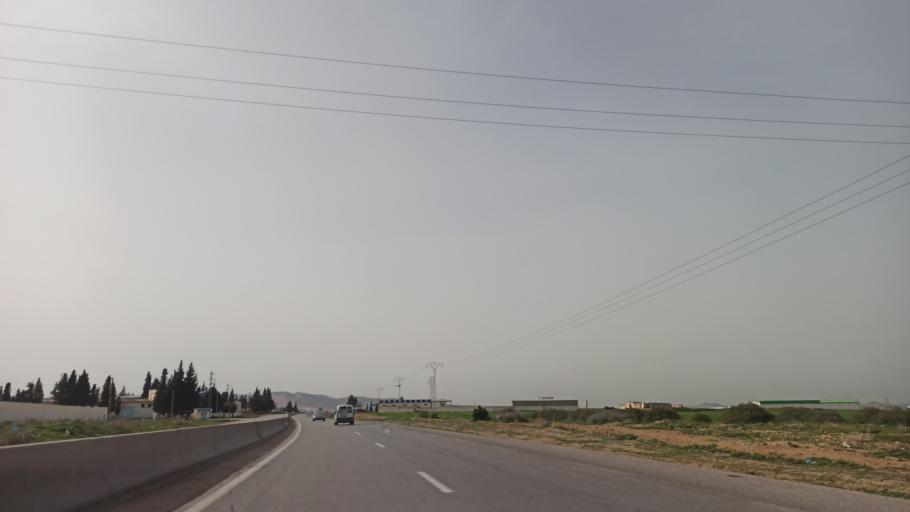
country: TN
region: Tunis
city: La Mohammedia
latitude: 36.5773
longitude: 10.0919
